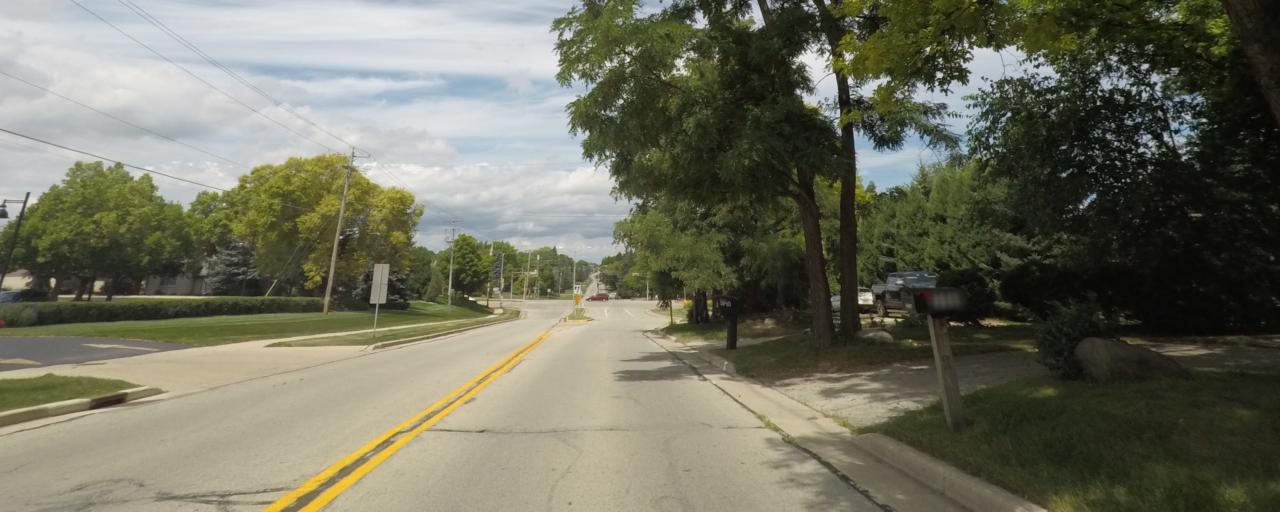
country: US
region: Wisconsin
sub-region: Waukesha County
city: New Berlin
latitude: 42.9869
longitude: -88.0684
